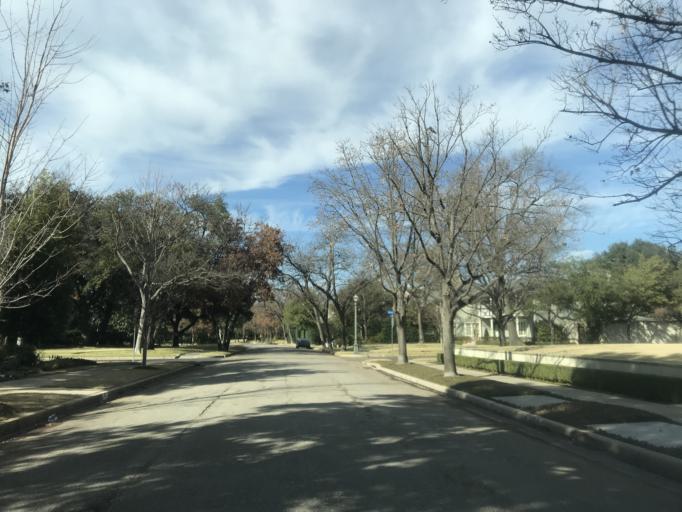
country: US
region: Texas
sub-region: Dallas County
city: Highland Park
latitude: 32.8251
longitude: -96.7932
